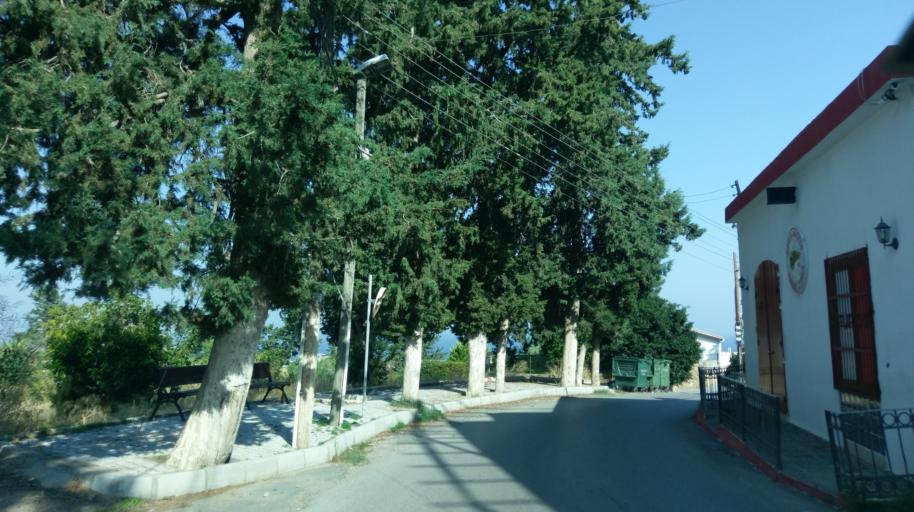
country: CY
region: Keryneia
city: Kyrenia
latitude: 35.3289
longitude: 33.2601
